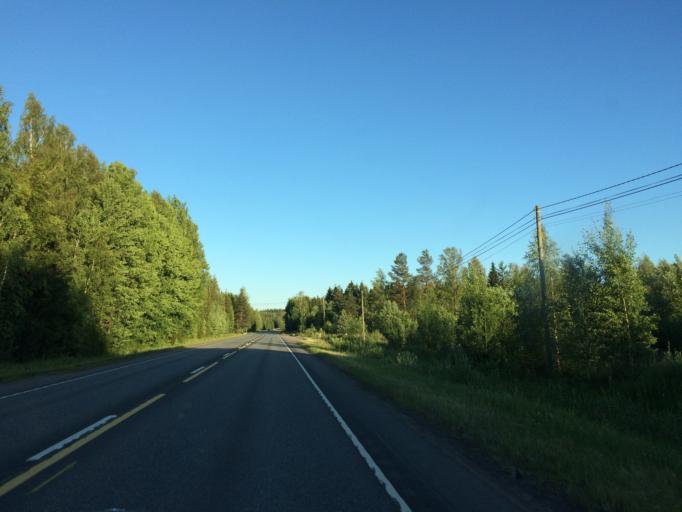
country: FI
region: Haeme
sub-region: Haemeenlinna
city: Tervakoski
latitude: 60.7767
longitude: 24.6956
